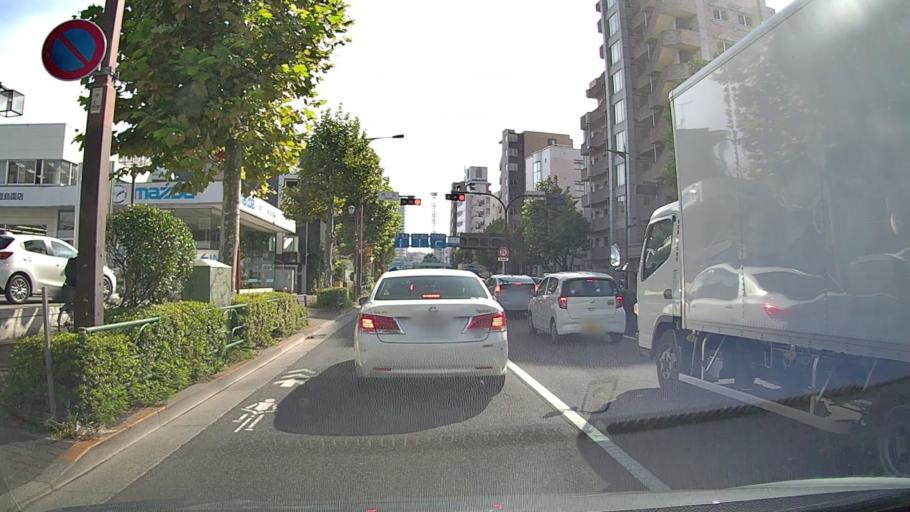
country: JP
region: Saitama
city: Wako
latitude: 35.7393
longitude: 139.6405
